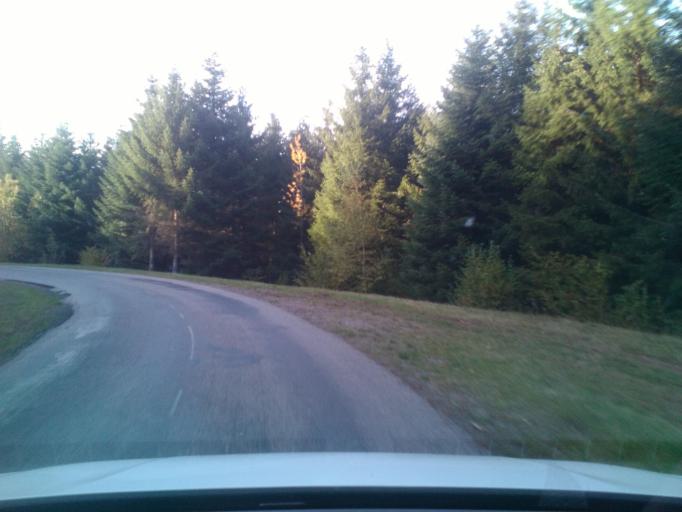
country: FR
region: Lorraine
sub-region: Departement des Vosges
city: Sainte-Marguerite
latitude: 48.3218
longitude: 7.0320
